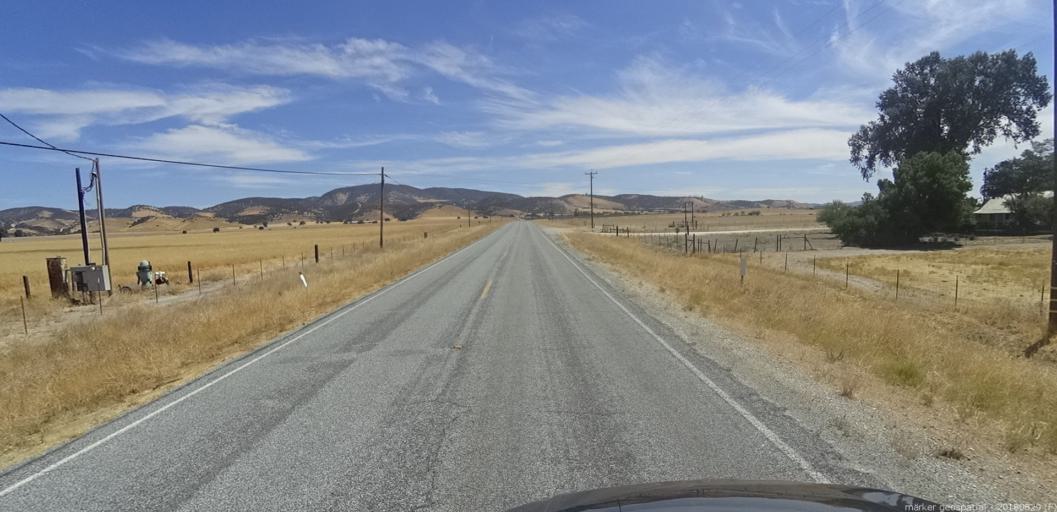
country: US
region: California
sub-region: Monterey County
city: King City
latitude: 35.9368
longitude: -121.0696
